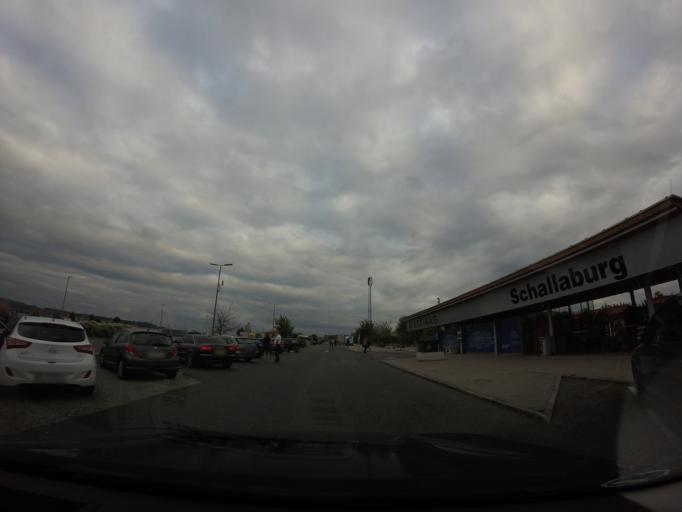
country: AT
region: Lower Austria
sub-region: Politischer Bezirk Melk
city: Loosdorf
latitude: 48.1949
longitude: 15.3794
